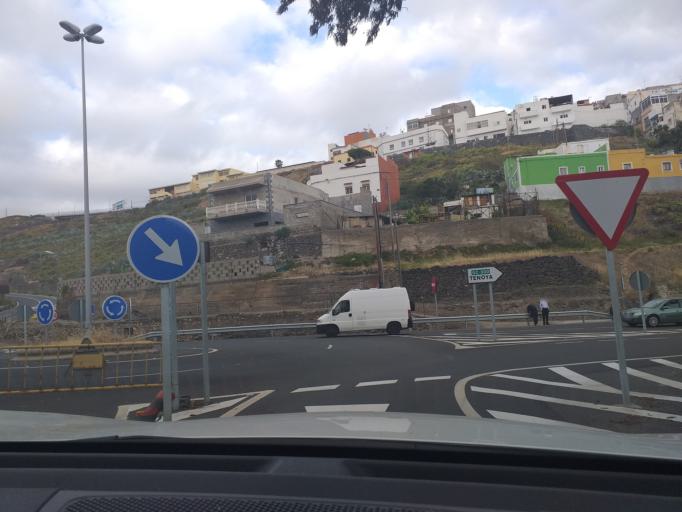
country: ES
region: Canary Islands
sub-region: Provincia de Las Palmas
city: Arucas
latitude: 28.1101
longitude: -15.4928
